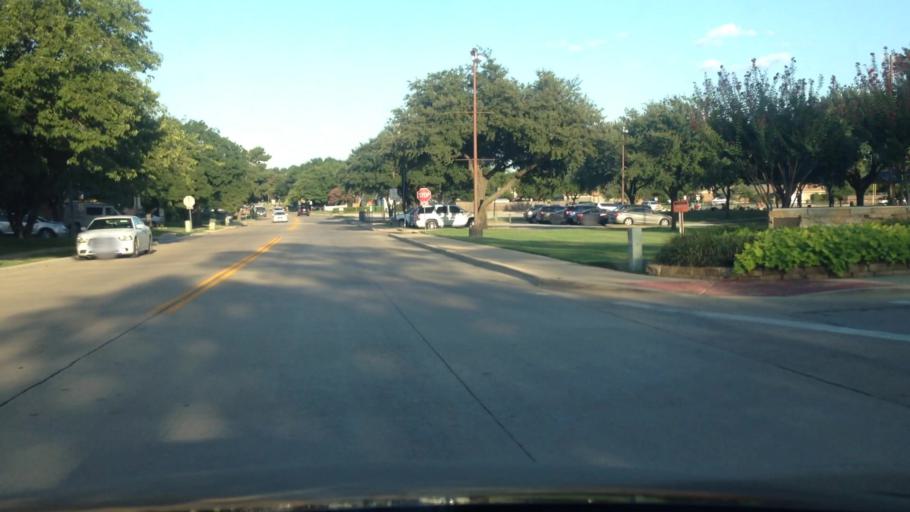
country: US
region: Texas
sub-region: Tarrant County
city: Watauga
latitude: 32.8816
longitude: -97.2418
